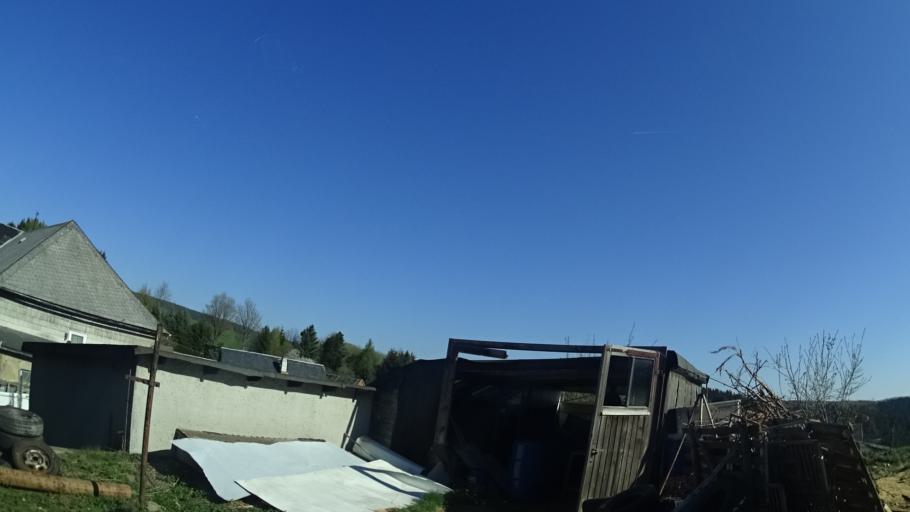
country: DE
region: Thuringia
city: Bohlen
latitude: 50.6019
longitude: 11.0528
